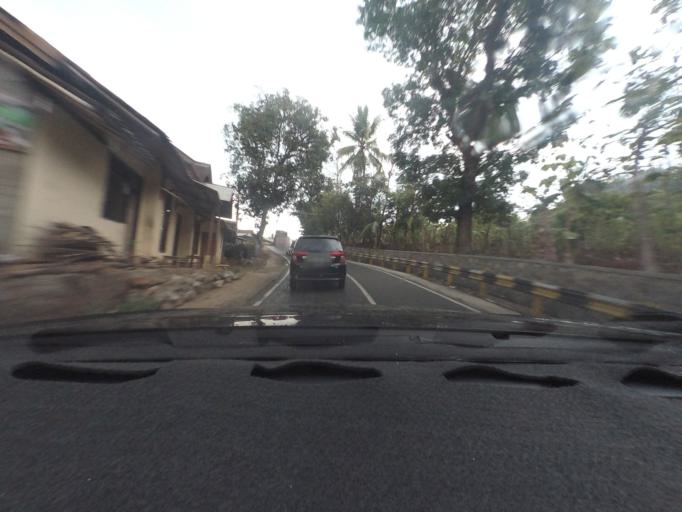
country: ID
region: West Java
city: Cilandak
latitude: -6.9812
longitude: 106.7083
